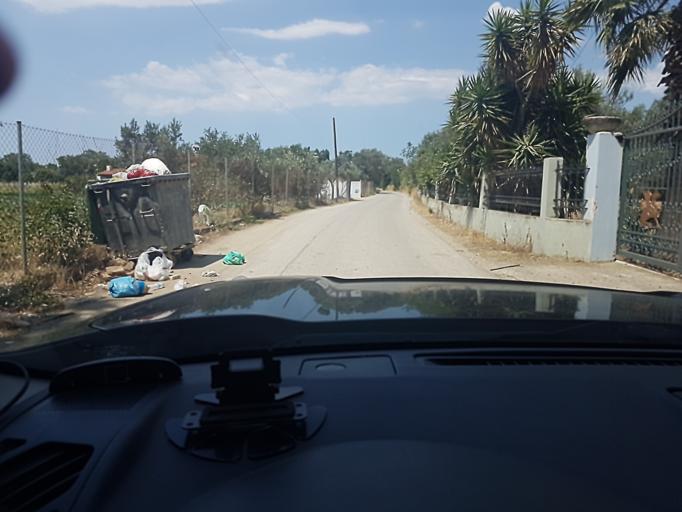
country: GR
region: Central Greece
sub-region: Nomos Evvoias
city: Ayios Nikolaos
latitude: 38.4136
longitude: 23.6597
